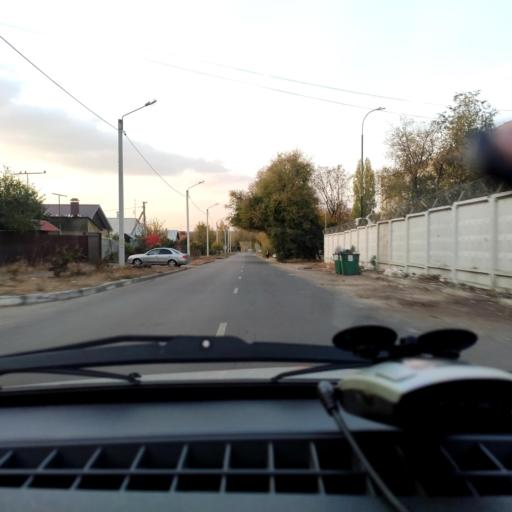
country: RU
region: Voronezj
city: Pridonskoy
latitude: 51.6601
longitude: 39.1259
